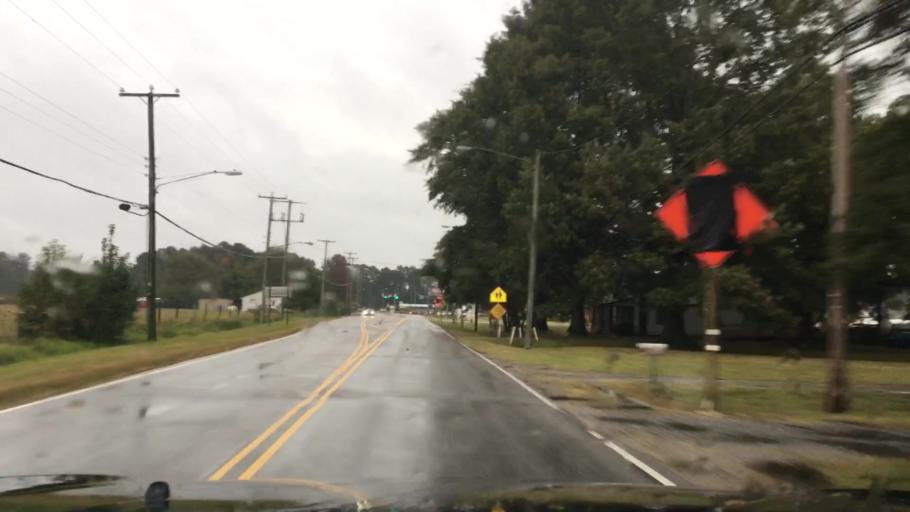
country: US
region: Virginia
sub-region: City of Chesapeake
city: Chesapeake
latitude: 36.6736
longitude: -76.2268
